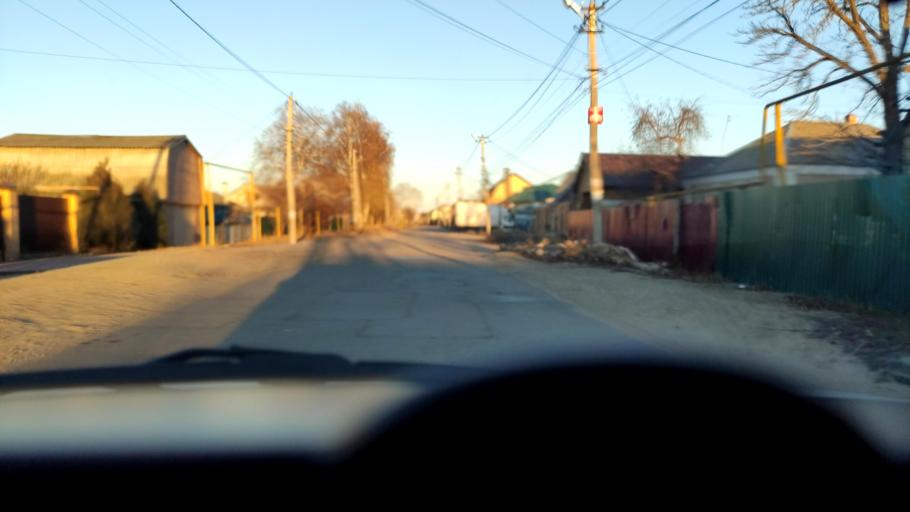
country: RU
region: Voronezj
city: Podgornoye
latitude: 51.7371
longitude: 39.1569
